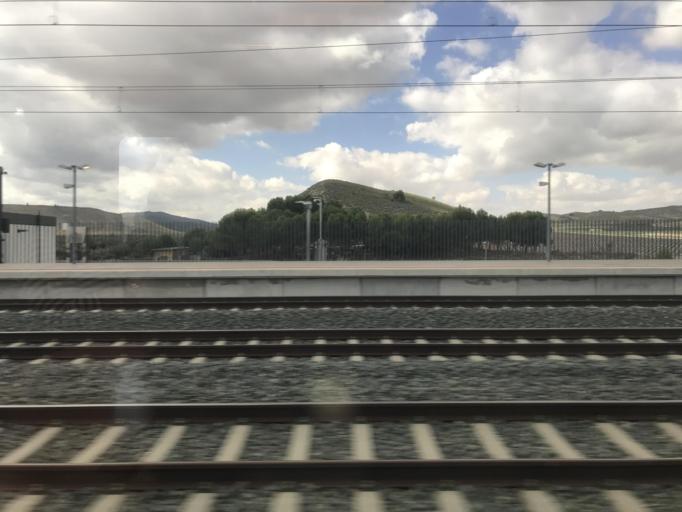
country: ES
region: Valencia
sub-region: Provincia de Alicante
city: Villena
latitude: 38.5864
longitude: -0.8746
